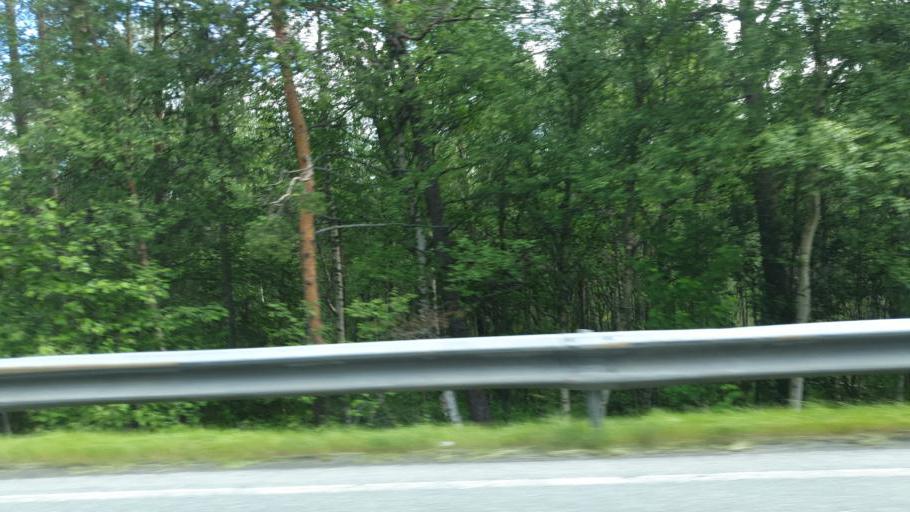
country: NO
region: Sor-Trondelag
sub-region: Rennebu
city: Berkak
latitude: 62.6867
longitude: 9.9306
